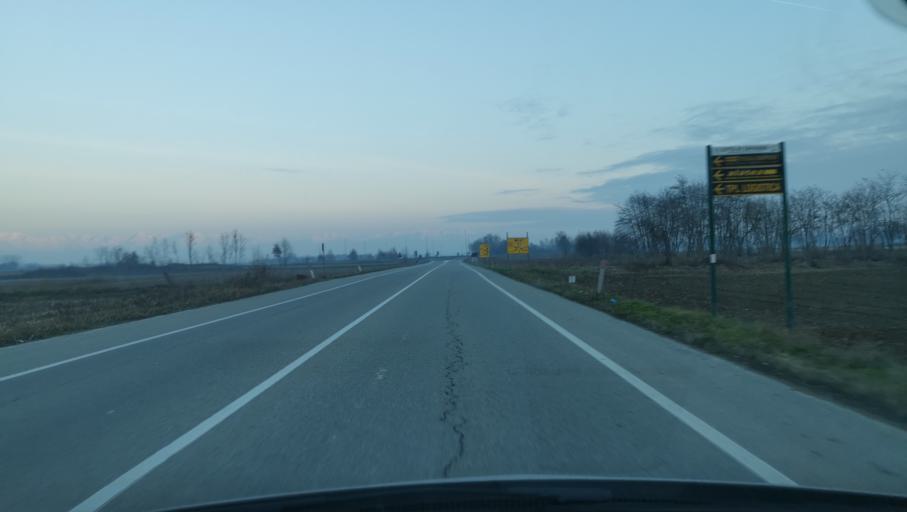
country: IT
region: Piedmont
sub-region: Provincia di Torino
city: Chivasso
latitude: 45.2256
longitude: 7.8908
